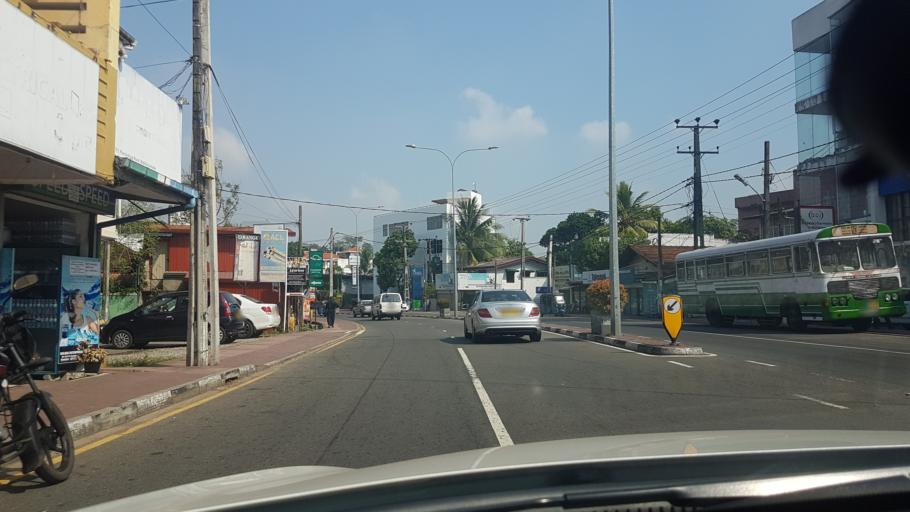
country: LK
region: Western
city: Battaramulla South
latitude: 6.8986
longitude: 79.9223
